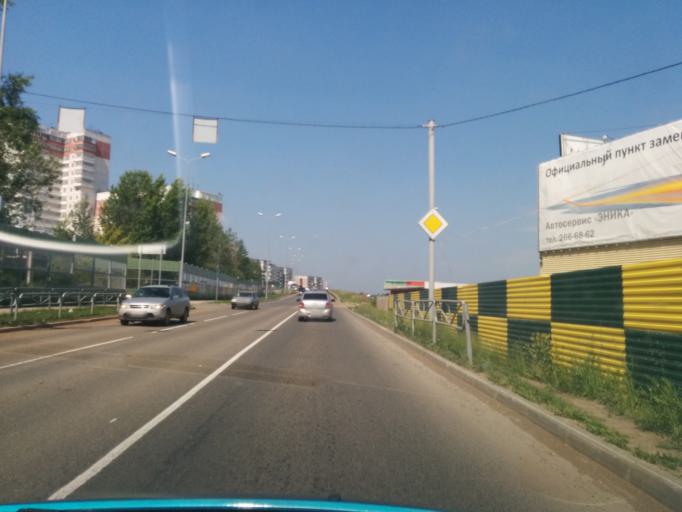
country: RU
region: Perm
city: Perm
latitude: 58.0021
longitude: 56.3137
